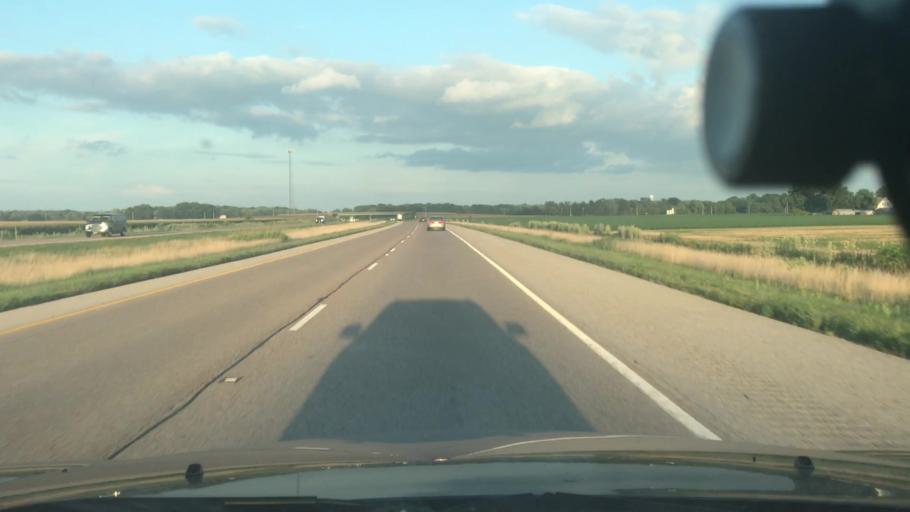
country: US
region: Illinois
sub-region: Clinton County
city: New Baden
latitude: 38.5137
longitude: -89.6574
